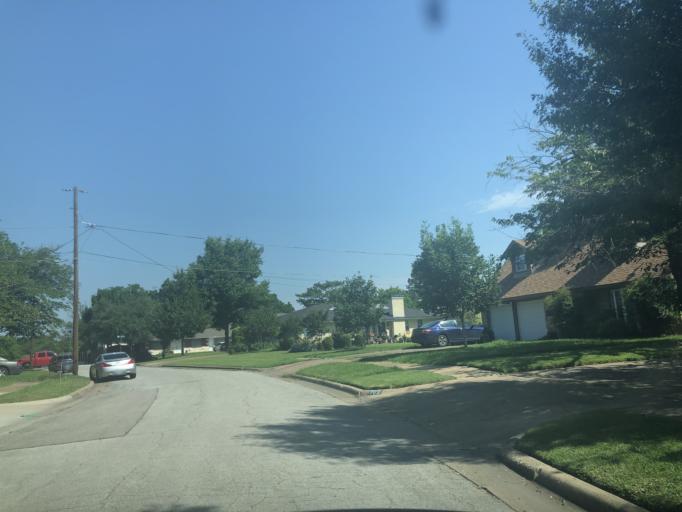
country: US
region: Texas
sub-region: Dallas County
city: Grand Prairie
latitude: 32.7212
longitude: -97.0035
